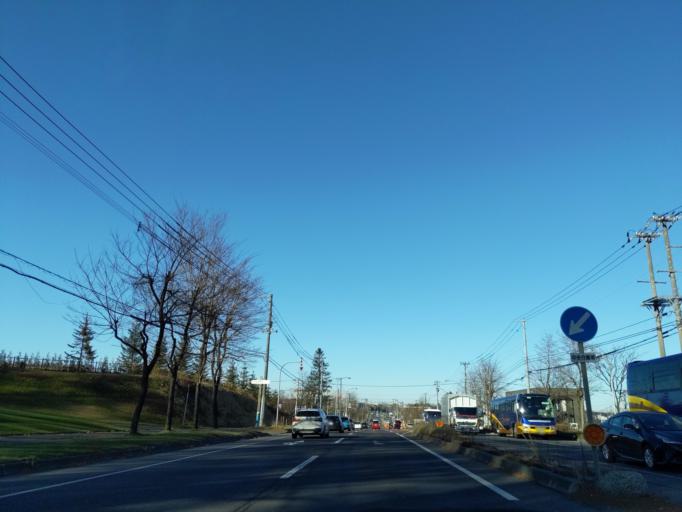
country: JP
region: Hokkaido
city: Kitahiroshima
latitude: 42.9468
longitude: 141.5003
